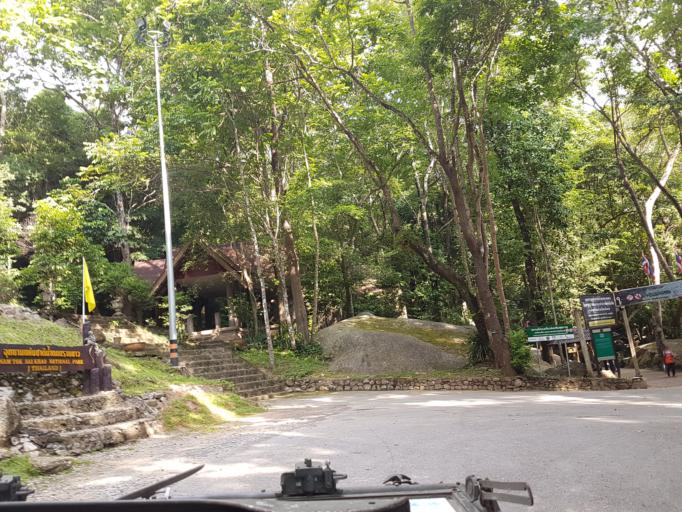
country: TH
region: Pattani
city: Khok Pho
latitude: 6.6570
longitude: 101.0958
